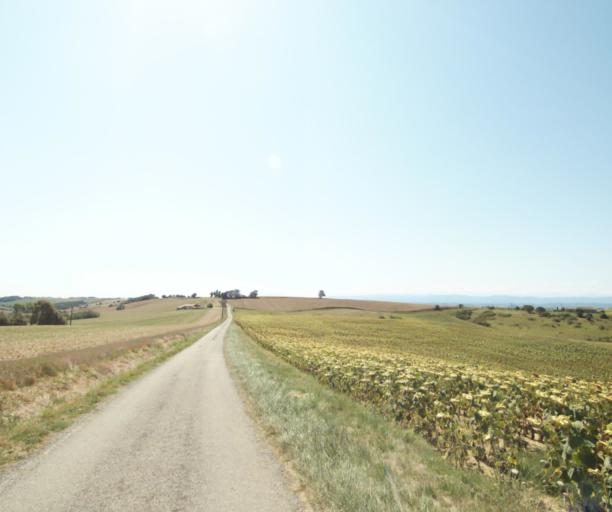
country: FR
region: Midi-Pyrenees
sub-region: Departement de l'Ariege
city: Lezat-sur-Leze
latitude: 43.2682
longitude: 1.3772
